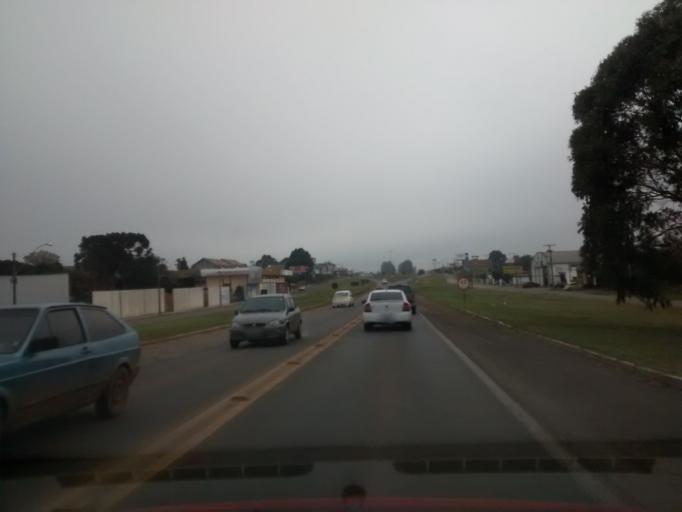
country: BR
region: Rio Grande do Sul
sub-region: Vacaria
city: Vacaria
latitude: -28.5036
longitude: -50.9230
